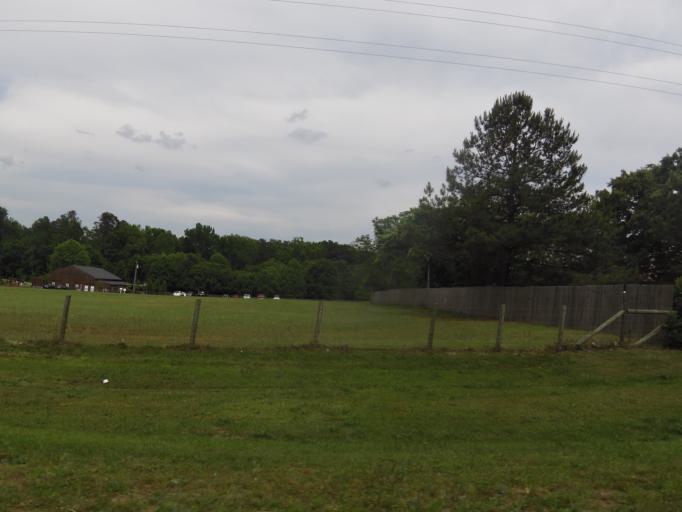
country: US
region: Georgia
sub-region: McDuffie County
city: Thomson
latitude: 33.4144
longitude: -82.4822
